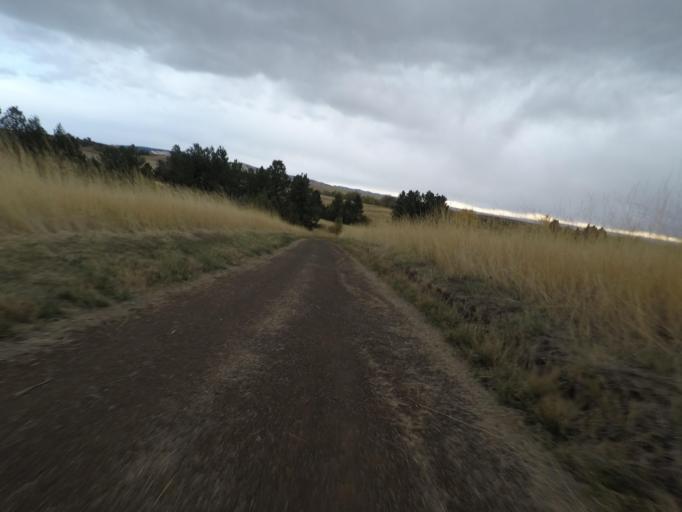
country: US
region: Washington
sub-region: Walla Walla County
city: Walla Walla East
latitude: 46.0690
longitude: -118.2568
